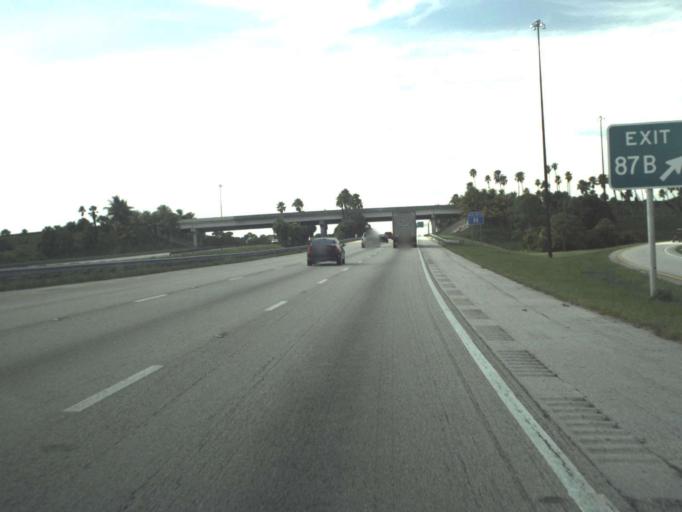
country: US
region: Florida
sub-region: Palm Beach County
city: Limestone Creek
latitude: 26.9391
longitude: -80.1516
